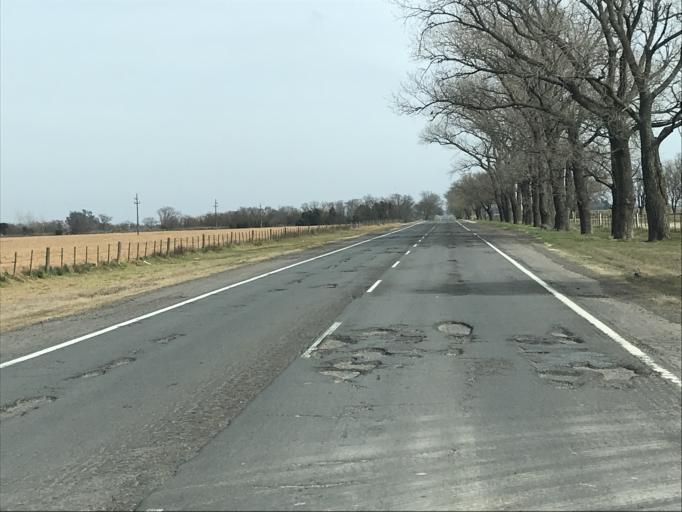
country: AR
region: Santa Fe
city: Armstrong
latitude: -32.7573
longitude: -61.7026
